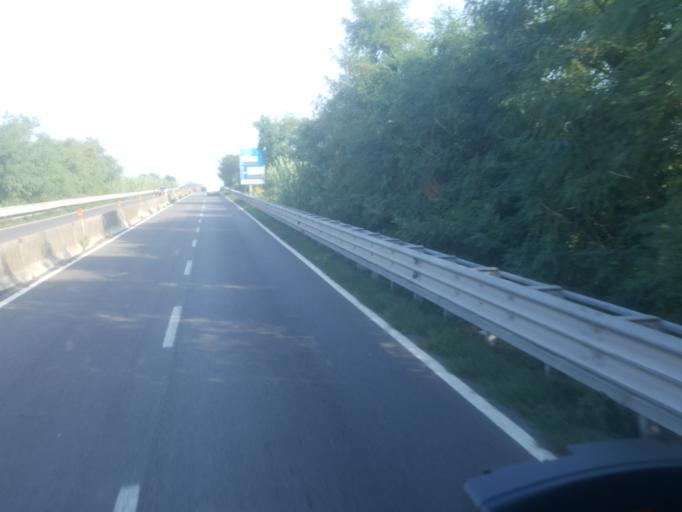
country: IT
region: Emilia-Romagna
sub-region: Provincia di Ravenna
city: Madonna Dell'Albero
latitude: 44.3909
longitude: 12.1867
